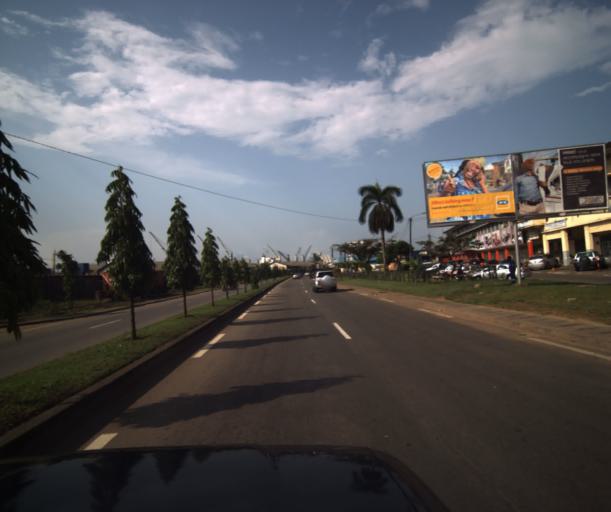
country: CM
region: Littoral
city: Douala
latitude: 4.0507
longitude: 9.6908
